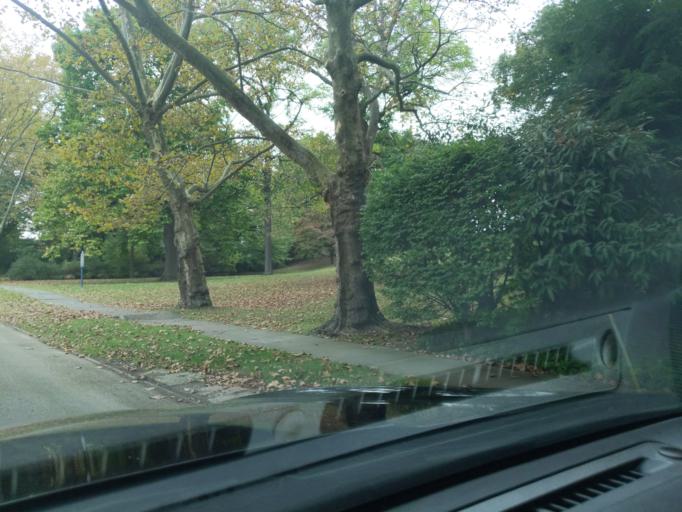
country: US
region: Pennsylvania
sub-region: Blair County
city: Lakemont
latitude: 40.4899
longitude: -78.4075
